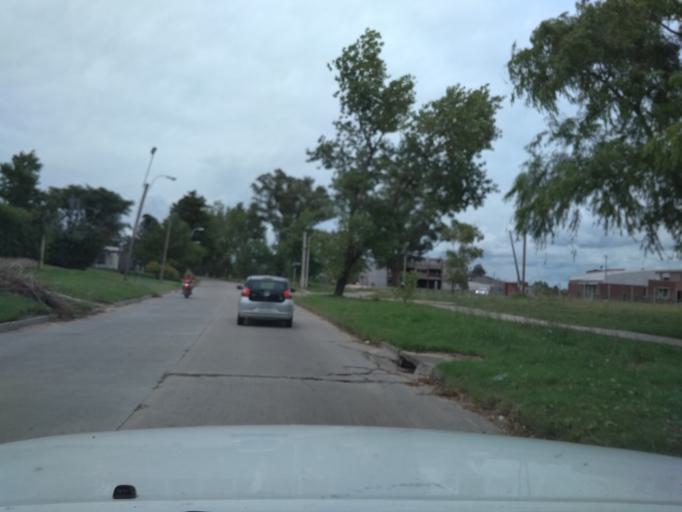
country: UY
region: Canelones
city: Paso de Carrasco
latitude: -34.8722
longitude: -56.0585
